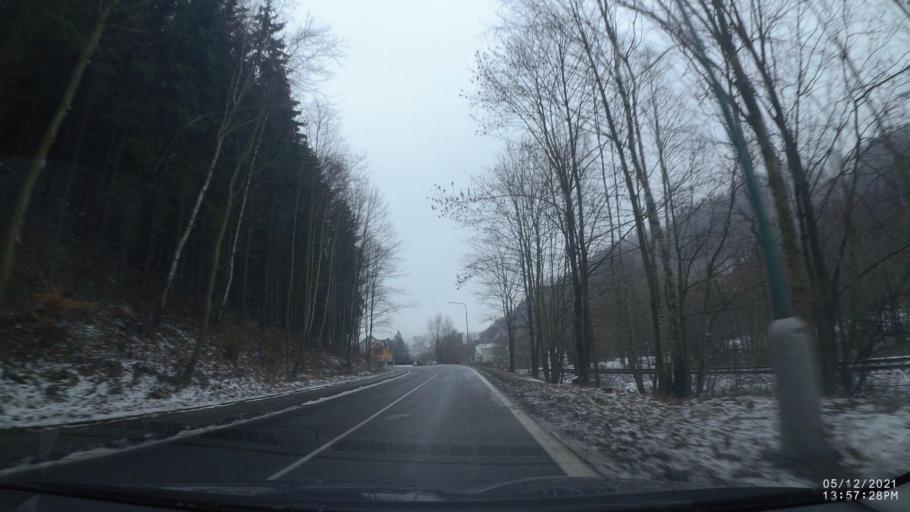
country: CZ
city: Hronov
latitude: 50.4874
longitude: 16.1832
